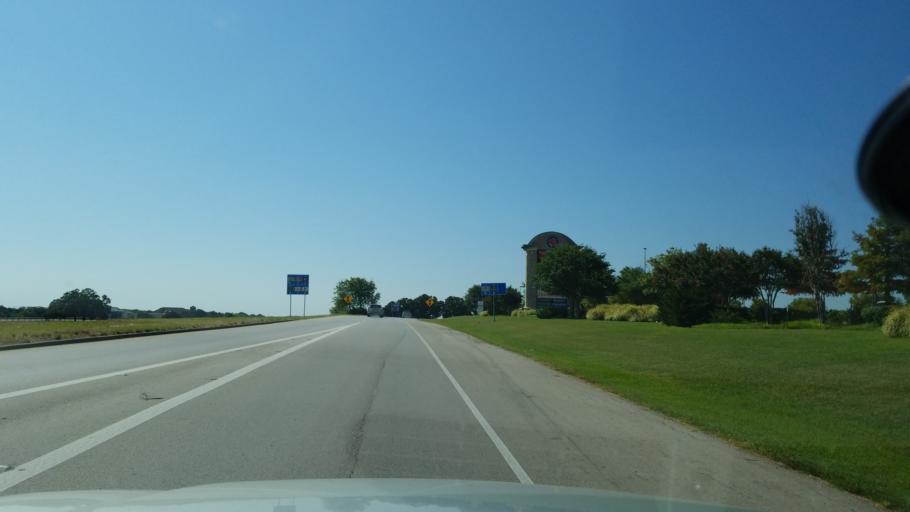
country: US
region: Texas
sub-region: Tarrant County
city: Mansfield
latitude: 32.5995
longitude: -97.1499
